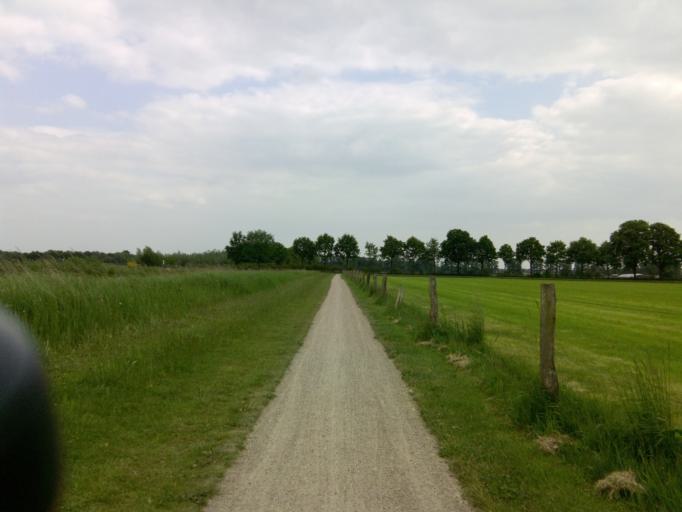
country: NL
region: Gelderland
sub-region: Berkelland
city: Borculo
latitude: 52.0773
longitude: 6.5165
